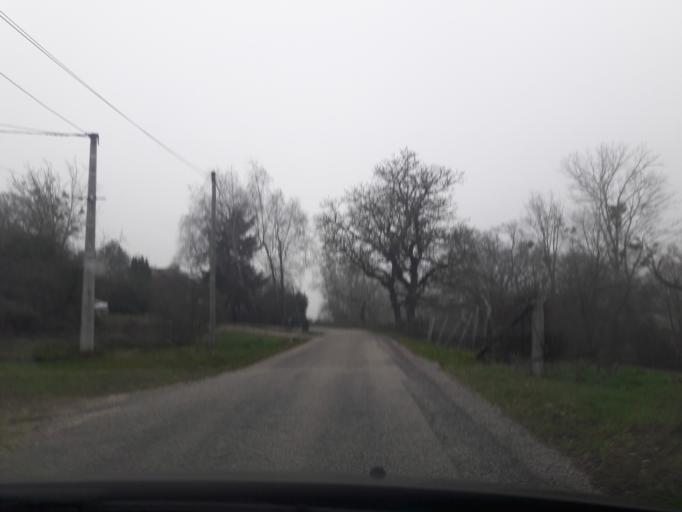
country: FR
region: Rhone-Alpes
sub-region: Departement de l'Isere
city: Chatonnay
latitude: 45.4209
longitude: 5.1585
